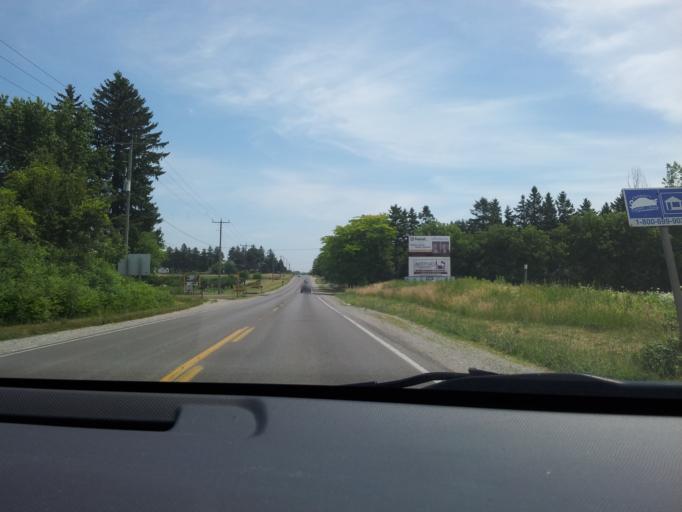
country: CA
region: Ontario
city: Norfolk County
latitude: 42.7926
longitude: -80.2404
